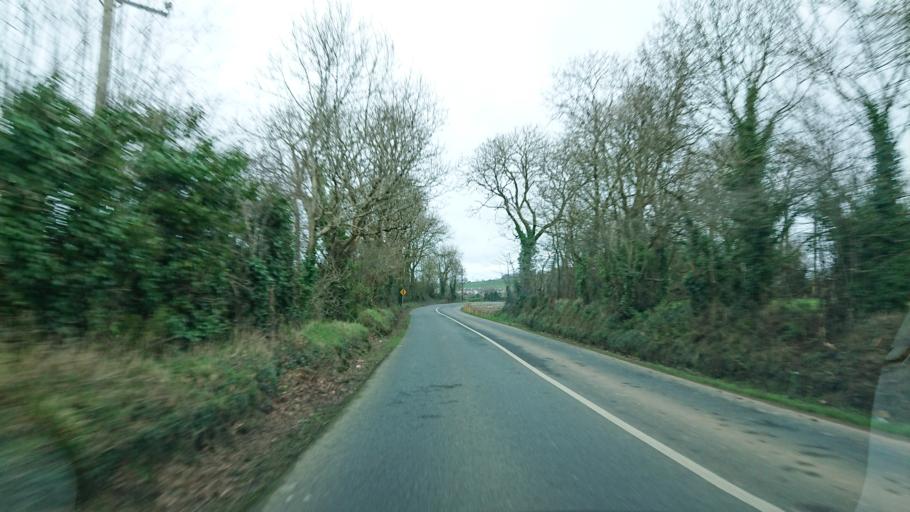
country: IE
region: Leinster
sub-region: Kilkenny
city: Mooncoin
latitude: 52.2237
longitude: -7.2389
